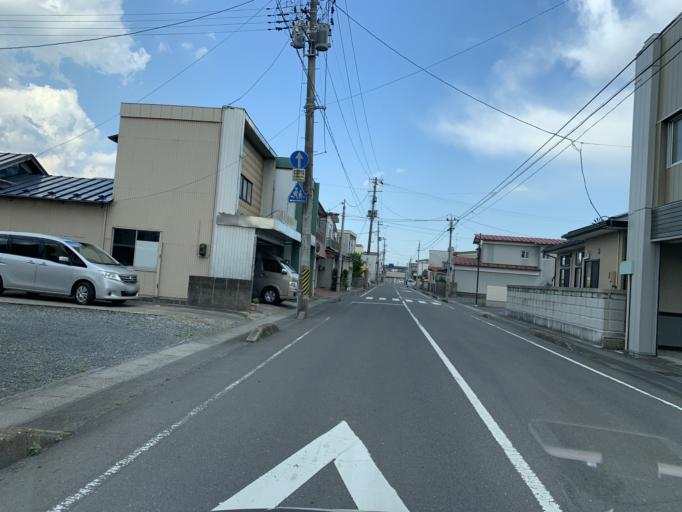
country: JP
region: Miyagi
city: Wakuya
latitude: 38.6295
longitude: 141.1969
